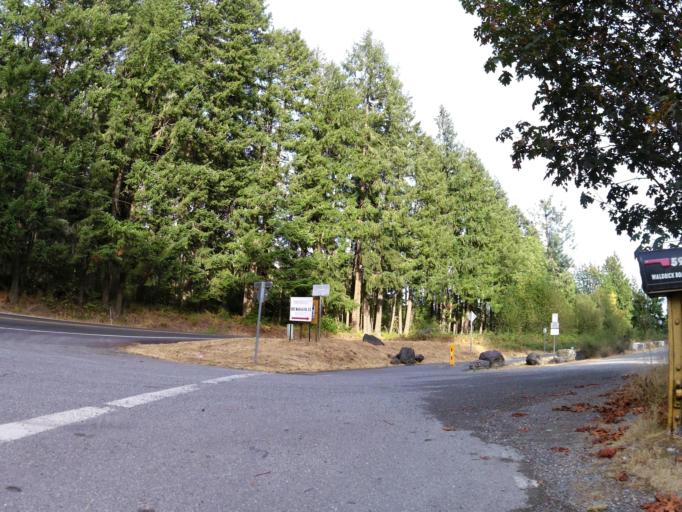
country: US
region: Washington
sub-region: Thurston County
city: Tenino
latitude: 46.9216
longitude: -122.8053
